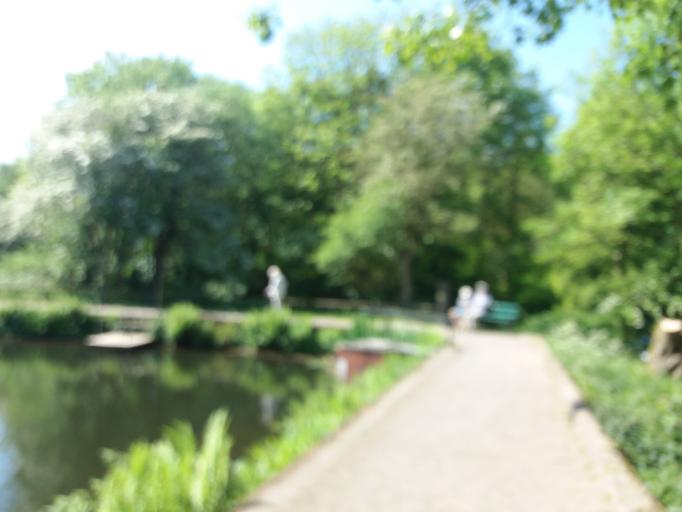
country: GB
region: England
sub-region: Lancashire
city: Coppull
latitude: 53.6314
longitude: -2.6507
